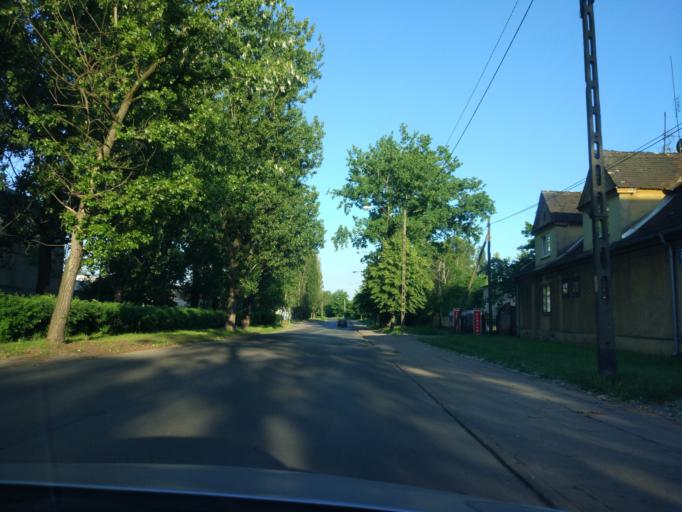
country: PL
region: Lodz Voivodeship
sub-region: Powiat kutnowski
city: Kutno
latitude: 52.2262
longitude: 19.3538
